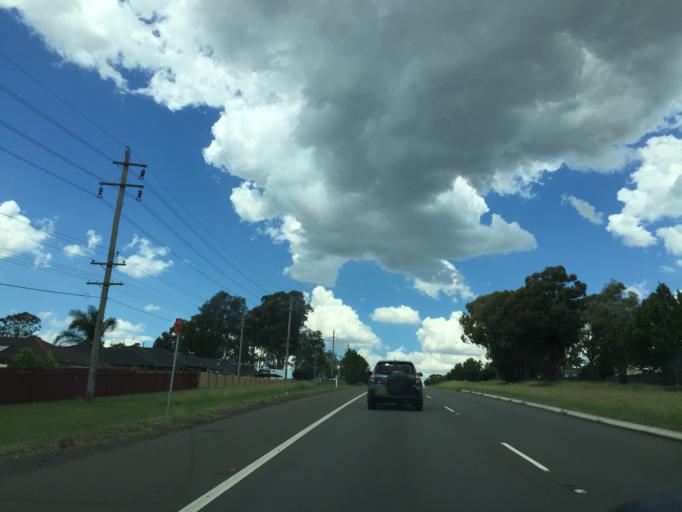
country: AU
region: New South Wales
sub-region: Blacktown
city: Mount Druitt
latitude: -33.7838
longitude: 150.8341
